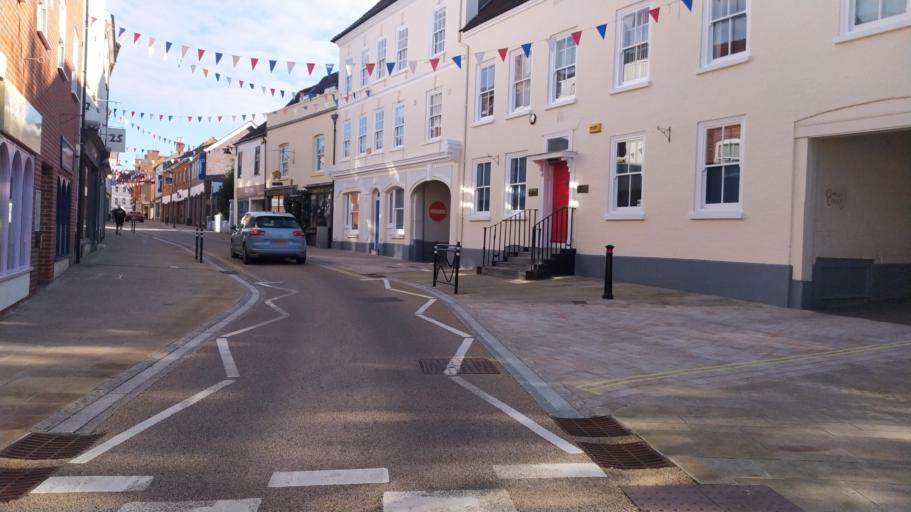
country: GB
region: England
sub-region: Hampshire
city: Romsey
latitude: 50.9876
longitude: -1.4995
